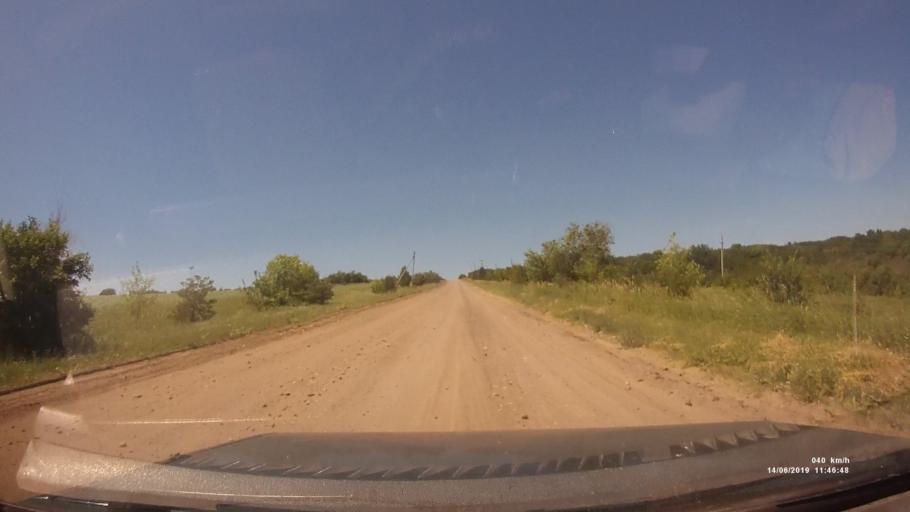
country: RU
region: Rostov
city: Kazanskaya
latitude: 49.8510
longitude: 41.3014
